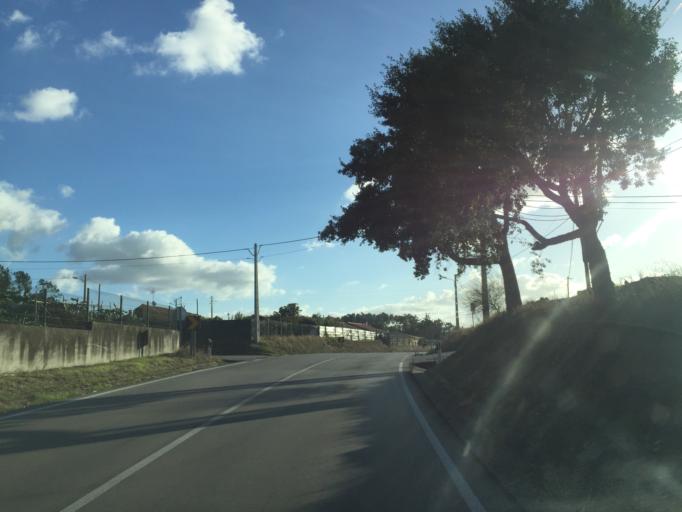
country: PT
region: Leiria
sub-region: Leiria
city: Monte Redondo
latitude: 39.9049
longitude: -8.8223
